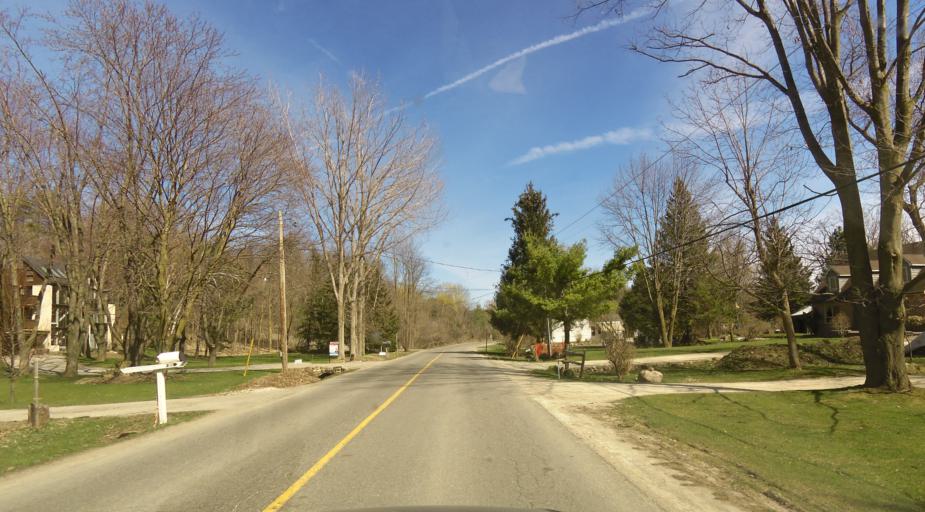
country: CA
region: Ontario
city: Brampton
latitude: 43.6471
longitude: -79.7755
